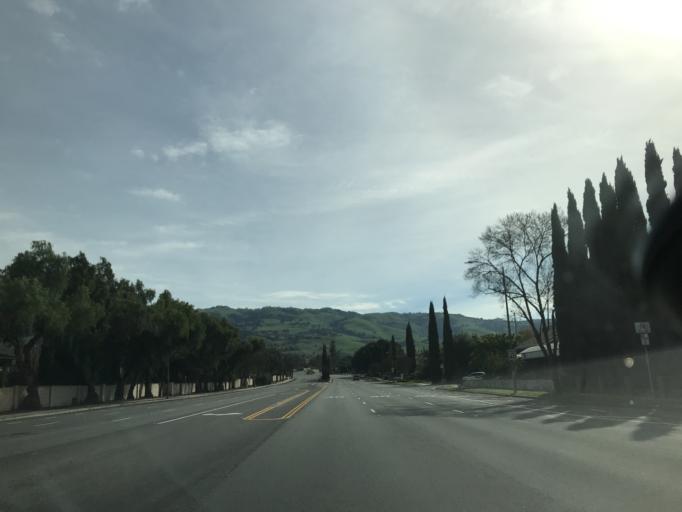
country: US
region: California
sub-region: Santa Clara County
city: Seven Trees
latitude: 37.3151
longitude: -121.7836
